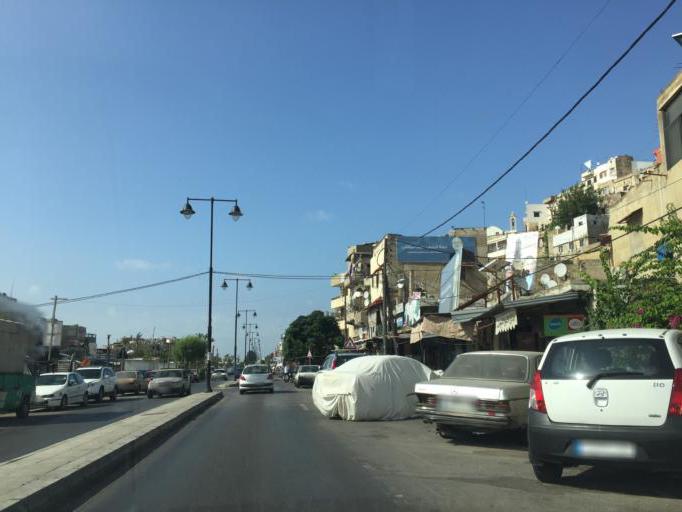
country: LB
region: Liban-Nord
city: Tripoli
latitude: 34.4358
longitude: 35.8469
